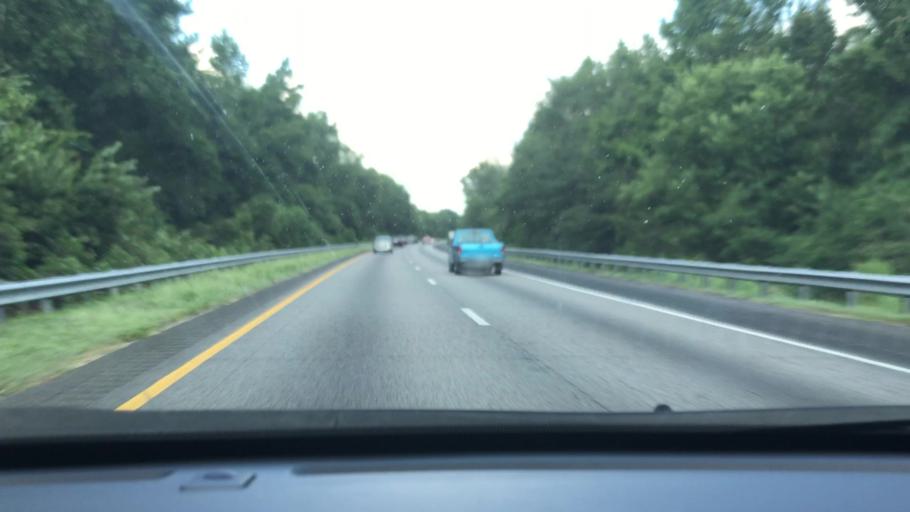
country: US
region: South Carolina
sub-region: Florence County
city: Florence
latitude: 34.2828
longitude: -79.6791
